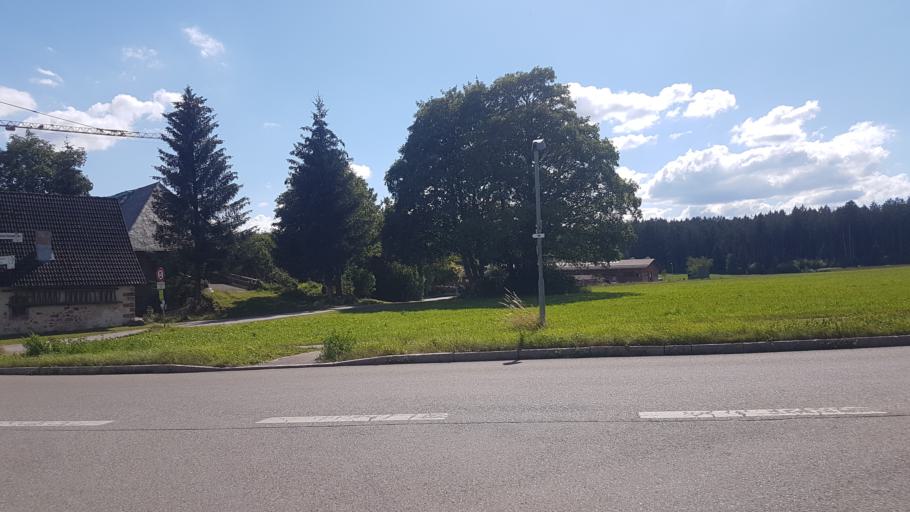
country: DE
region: Baden-Wuerttemberg
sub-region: Freiburg Region
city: Konigsfeld im Schwarzwald
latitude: 48.1437
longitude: 8.4032
